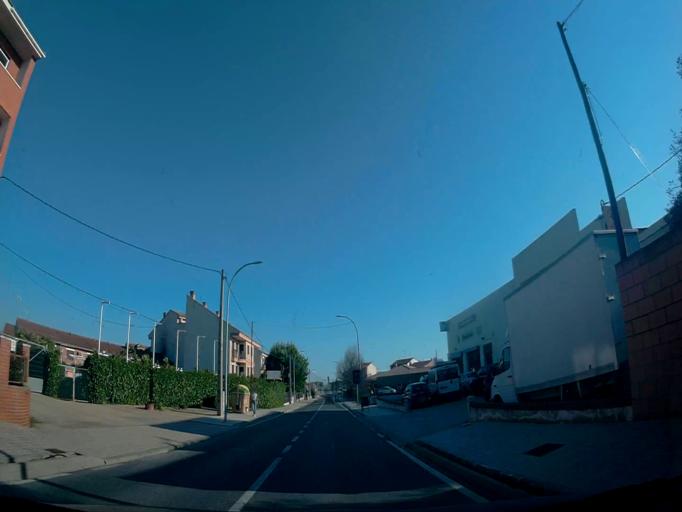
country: ES
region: Castille-La Mancha
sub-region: Province of Toledo
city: Almorox
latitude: 40.2315
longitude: -4.3920
